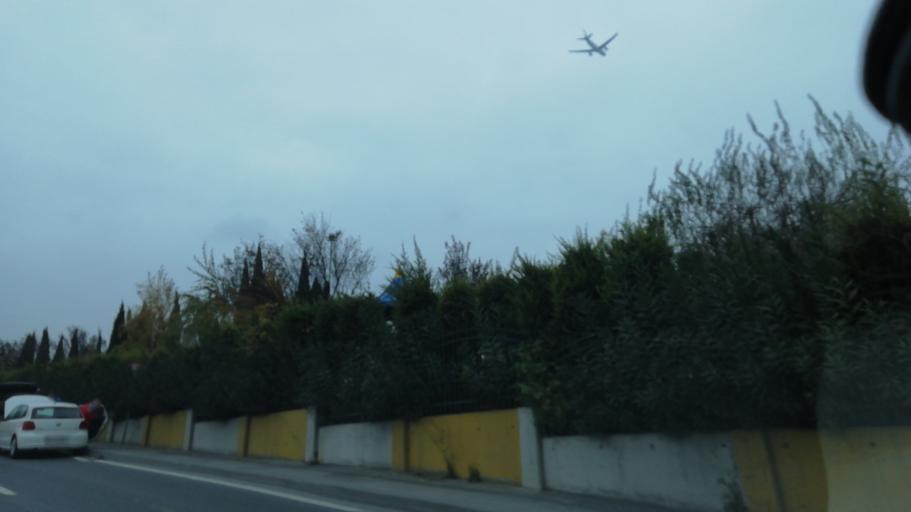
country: TR
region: Istanbul
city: Bahcelievler
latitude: 41.0005
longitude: 28.8081
